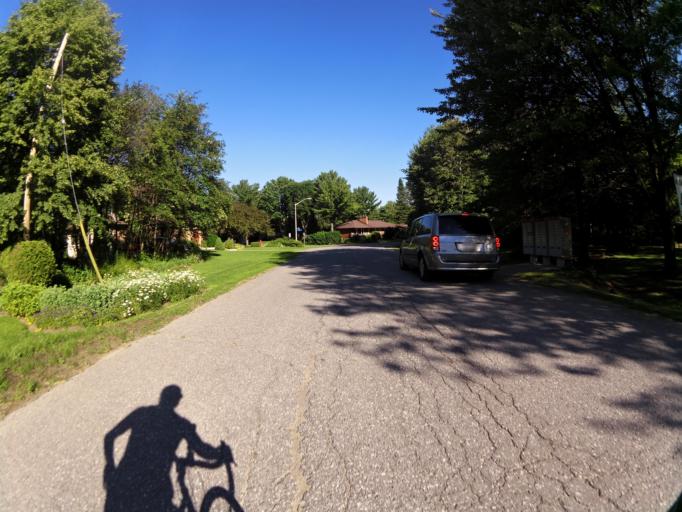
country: CA
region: Ontario
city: Bells Corners
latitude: 45.3160
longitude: -75.7307
